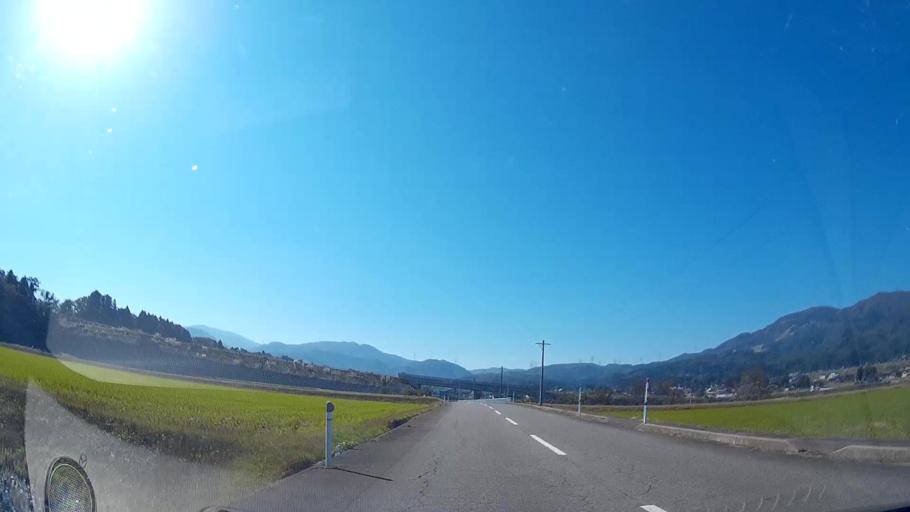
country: JP
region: Toyama
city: Fukumitsu
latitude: 36.5290
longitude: 136.8589
